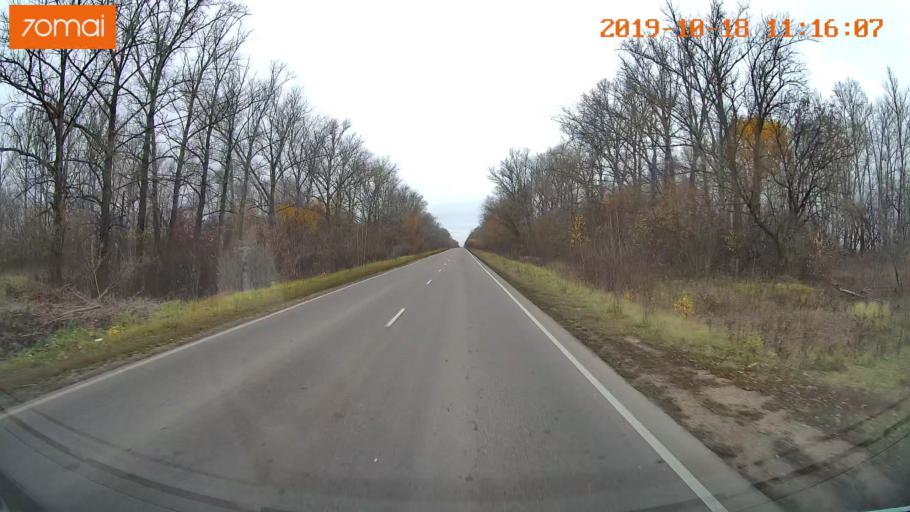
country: RU
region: Tula
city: Kimovsk
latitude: 54.0025
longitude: 38.5482
